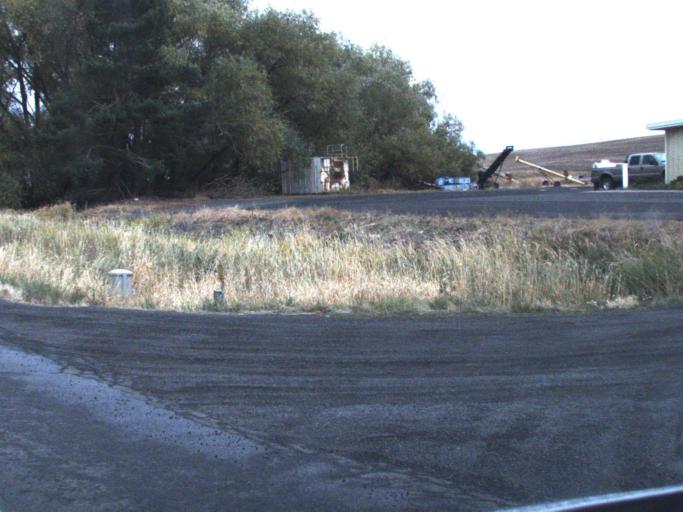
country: US
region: Washington
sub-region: Whitman County
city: Pullman
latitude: 46.7061
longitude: -117.2043
